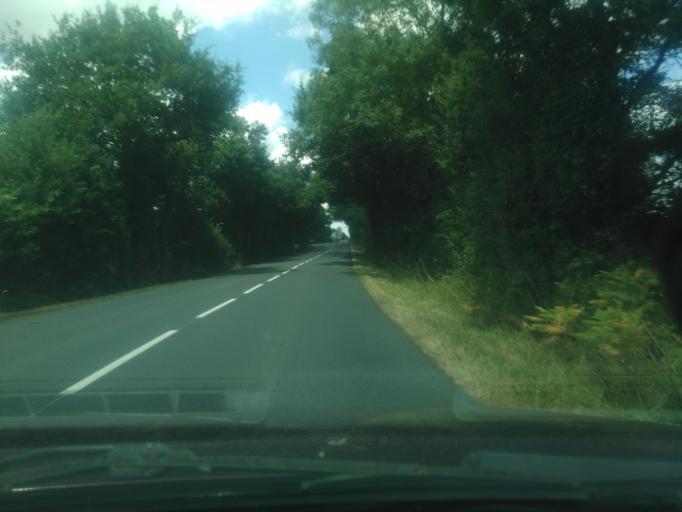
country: FR
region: Pays de la Loire
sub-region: Departement de la Vendee
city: Chauche
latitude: 46.8164
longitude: -1.2666
